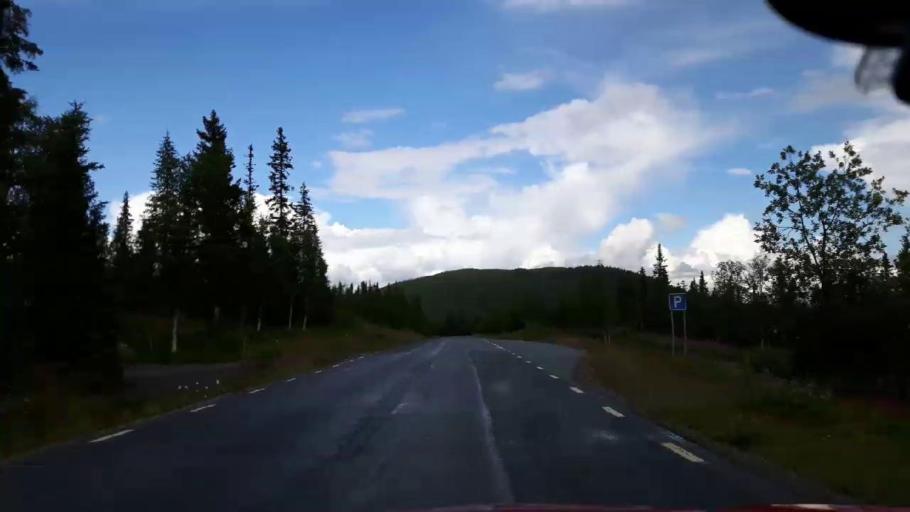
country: SE
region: Vaesterbotten
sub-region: Vilhelmina Kommun
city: Sjoberg
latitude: 65.0161
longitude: 15.1697
